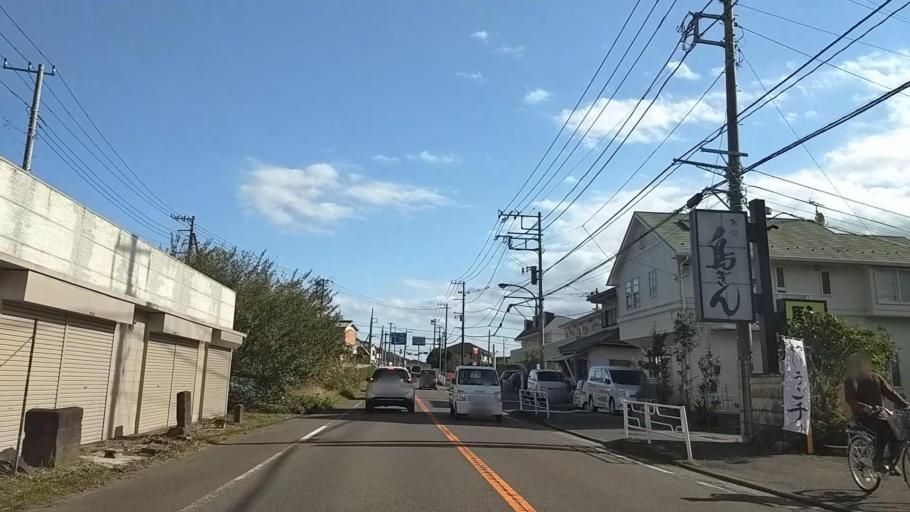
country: JP
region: Kanagawa
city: Odawara
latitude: 35.3058
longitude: 139.1851
